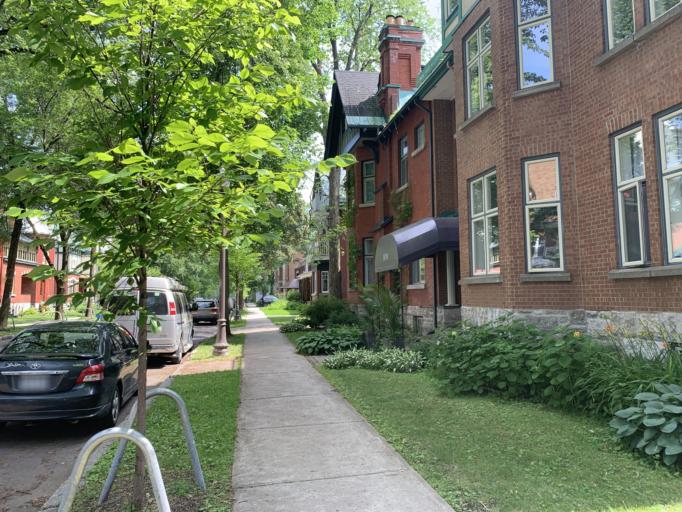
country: CA
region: Quebec
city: Quebec
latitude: 46.8011
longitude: -71.2298
